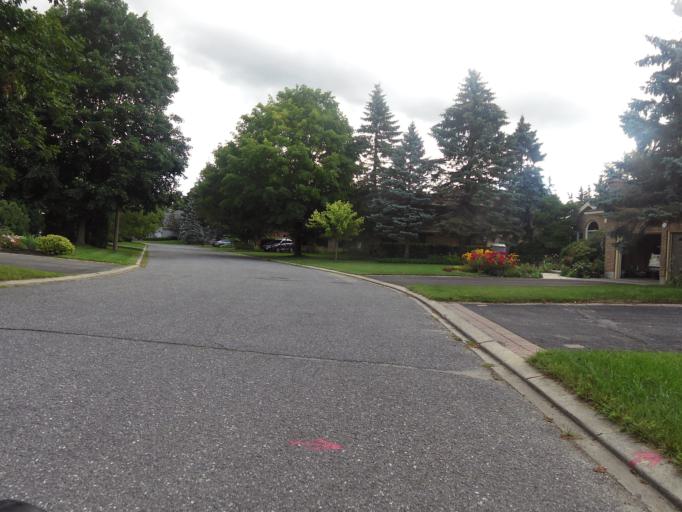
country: CA
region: Ontario
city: Bells Corners
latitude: 45.3231
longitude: -75.9102
